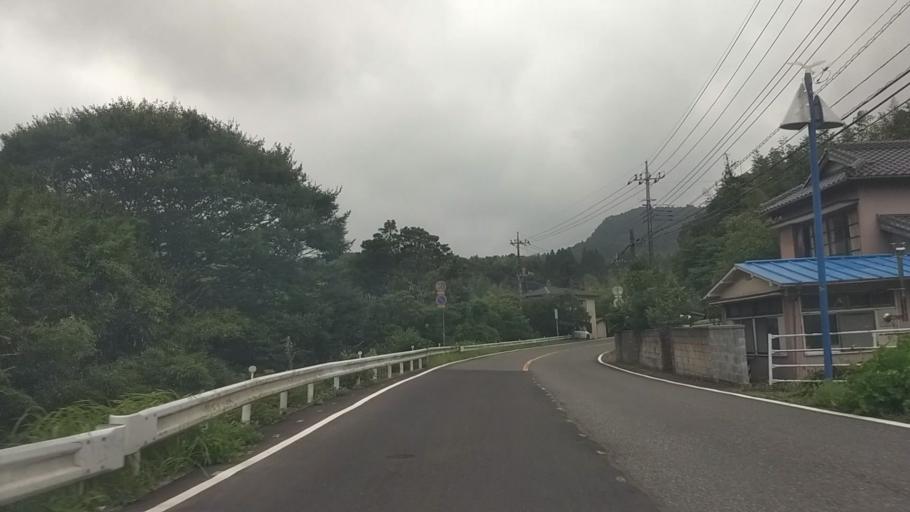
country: JP
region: Chiba
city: Kawaguchi
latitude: 35.1403
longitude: 139.9760
